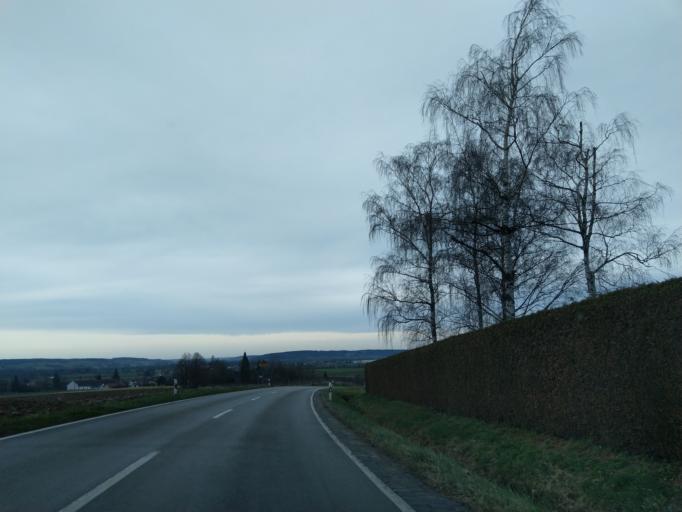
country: DE
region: Bavaria
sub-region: Lower Bavaria
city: Aldersbach
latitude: 48.6263
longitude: 13.0182
